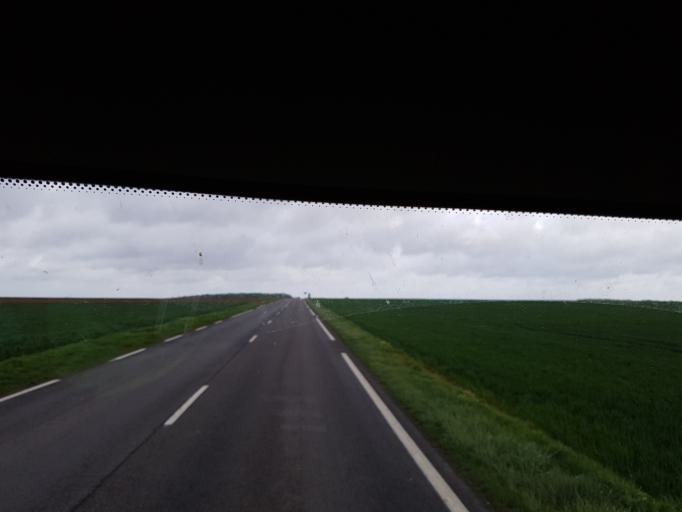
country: FR
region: Picardie
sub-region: Departement de l'Aisne
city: Crouy
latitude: 49.4241
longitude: 3.3484
